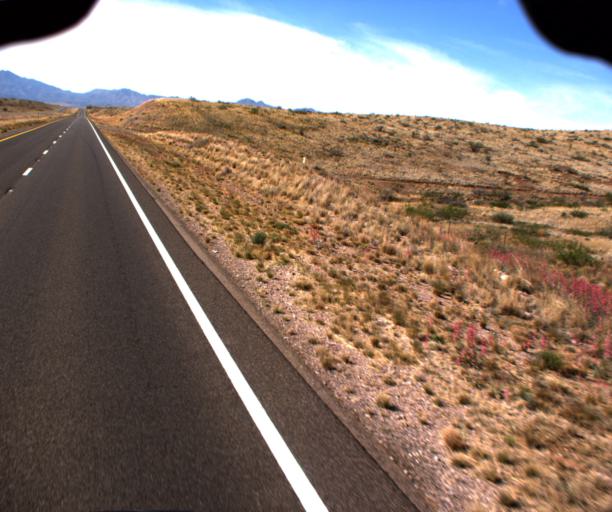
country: US
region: Arizona
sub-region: Cochise County
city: Willcox
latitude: 32.4250
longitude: -109.6631
